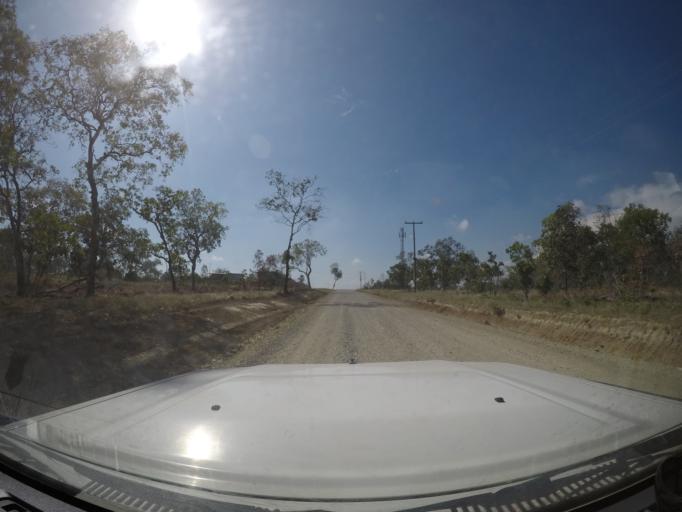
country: PG
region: Central Province
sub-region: Rigo
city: Kwikila
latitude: -9.9622
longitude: 147.6582
